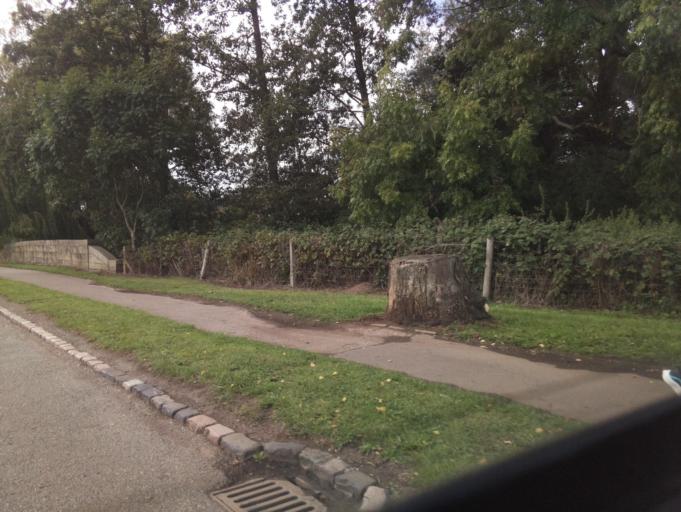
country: GB
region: England
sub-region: Staffordshire
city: Barlaston
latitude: 52.9534
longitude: -2.1625
